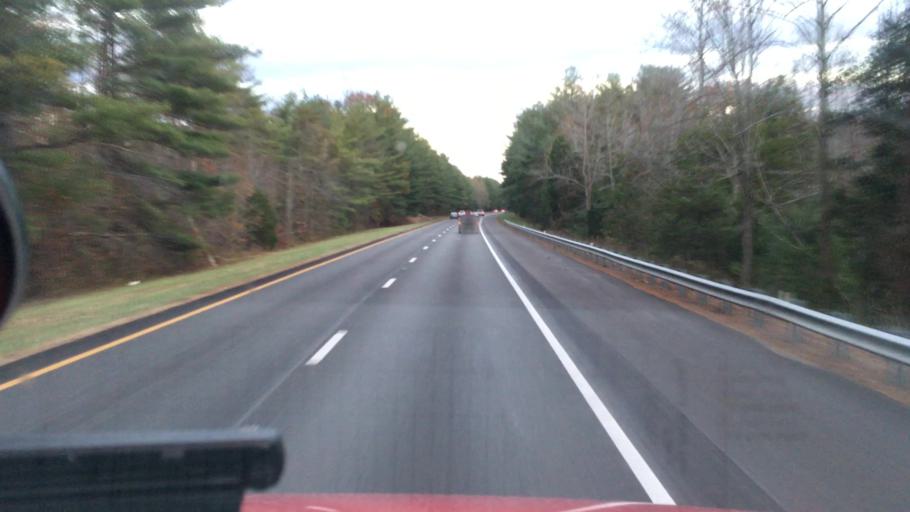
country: US
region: Virginia
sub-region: Fluvanna County
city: Palmyra
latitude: 37.9523
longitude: -78.1398
